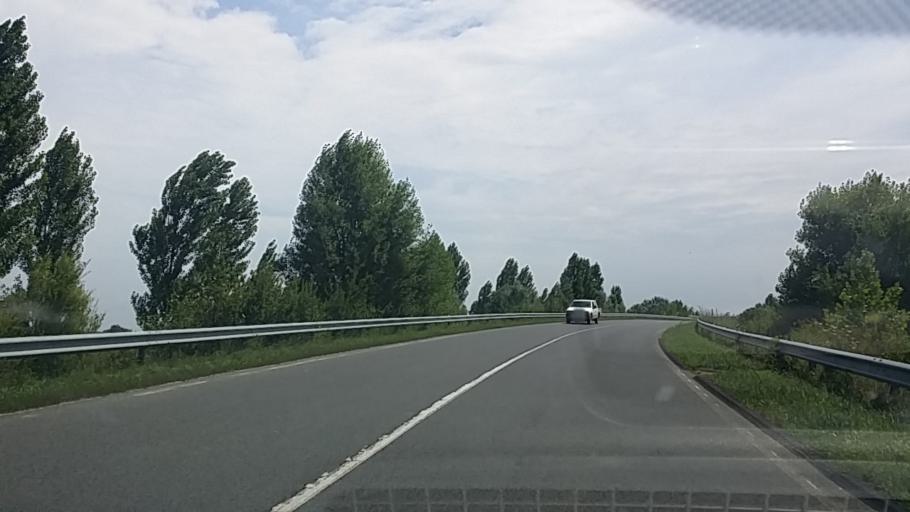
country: HU
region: Zala
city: Becsehely
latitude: 46.4191
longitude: 16.7628
